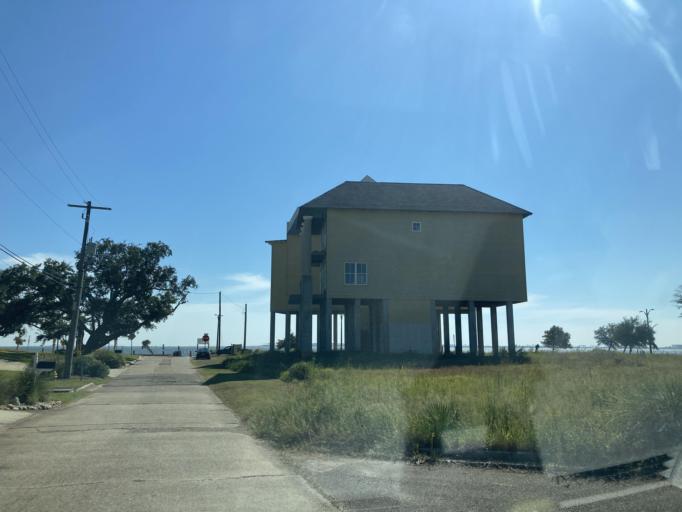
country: US
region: Mississippi
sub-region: Jackson County
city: Ocean Springs
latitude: 30.4083
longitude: -88.8333
